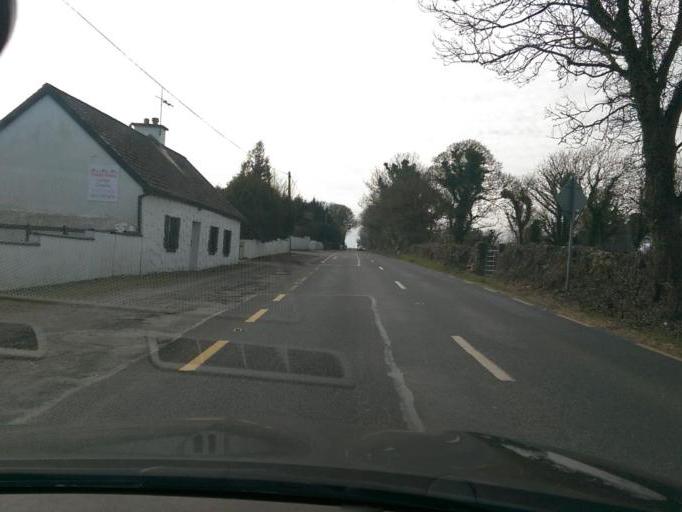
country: IE
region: Connaught
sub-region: County Galway
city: Claregalway
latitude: 53.3740
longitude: -8.8783
